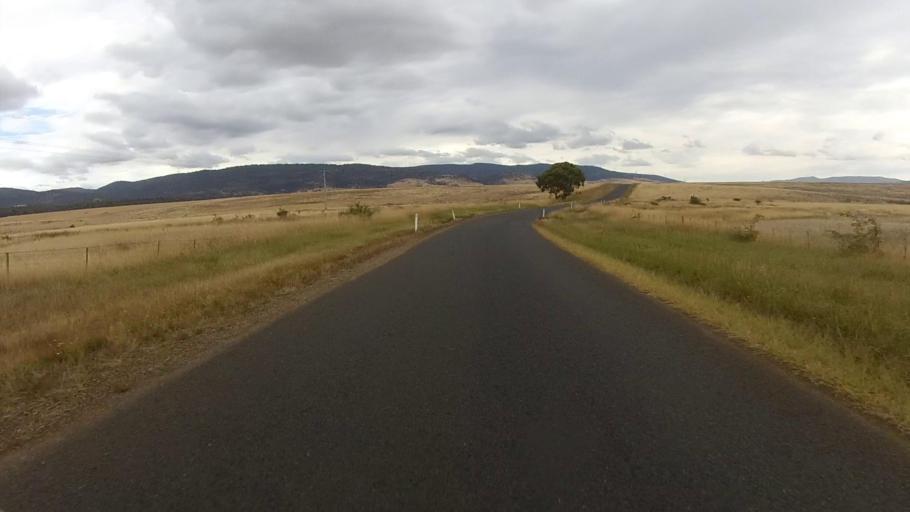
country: AU
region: Tasmania
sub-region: Northern Midlands
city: Evandale
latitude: -41.8273
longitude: 147.7894
